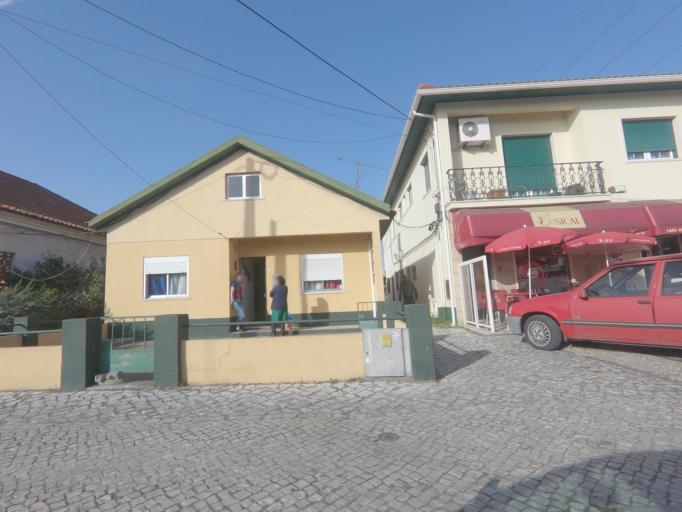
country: PT
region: Leiria
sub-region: Marinha Grande
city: Marinha Grande
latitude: 39.7491
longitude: -8.9184
